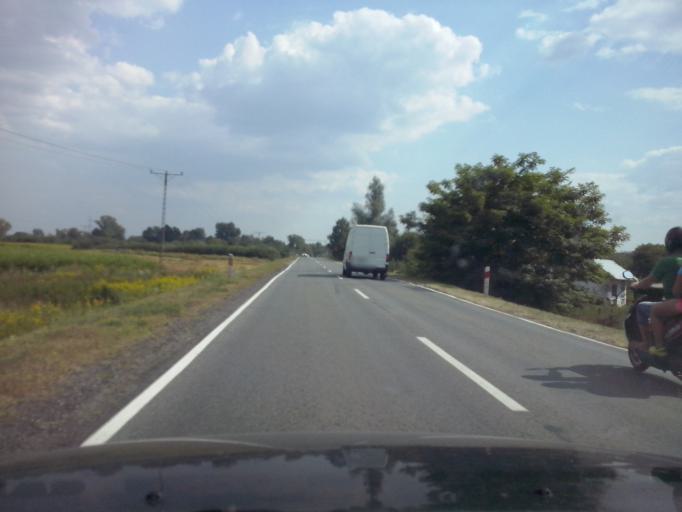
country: PL
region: Subcarpathian Voivodeship
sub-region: Powiat nizanski
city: Rudnik nad Sanem
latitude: 50.4488
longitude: 22.2499
